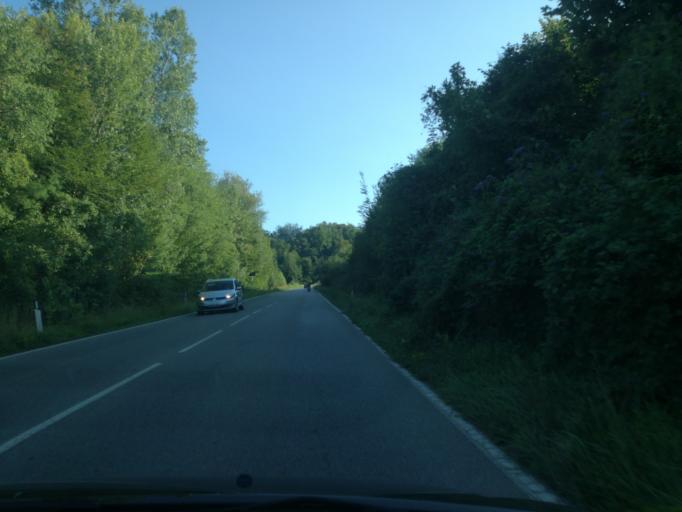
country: IT
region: Lombardy
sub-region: Provincia di Lecco
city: Imbersago
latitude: 45.7020
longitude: 9.4488
